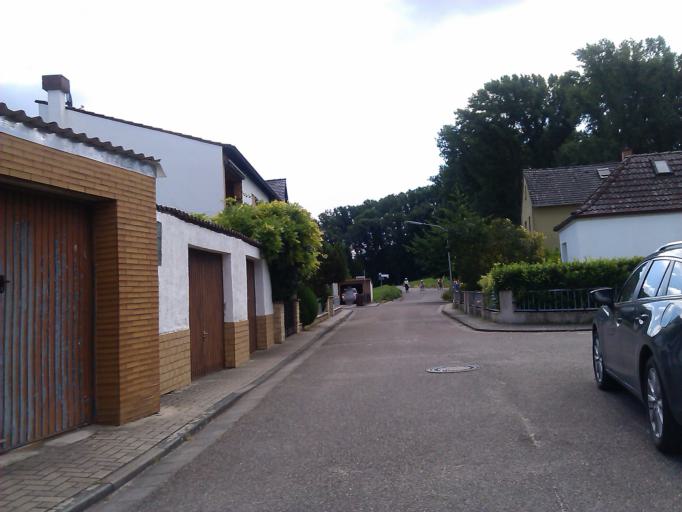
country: DE
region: Rheinland-Pfalz
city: Altrip
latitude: 49.4262
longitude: 8.4948
